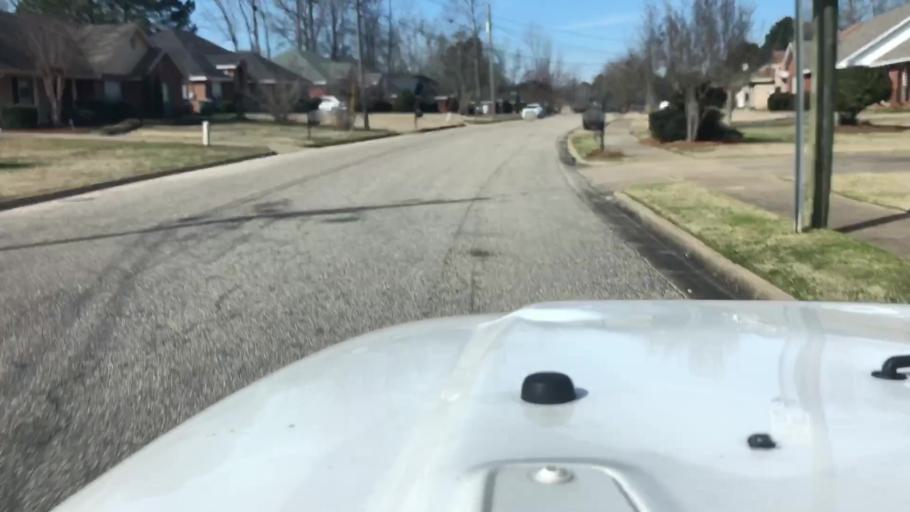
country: US
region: Alabama
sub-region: Elmore County
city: Blue Ridge
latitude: 32.4080
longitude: -86.1939
